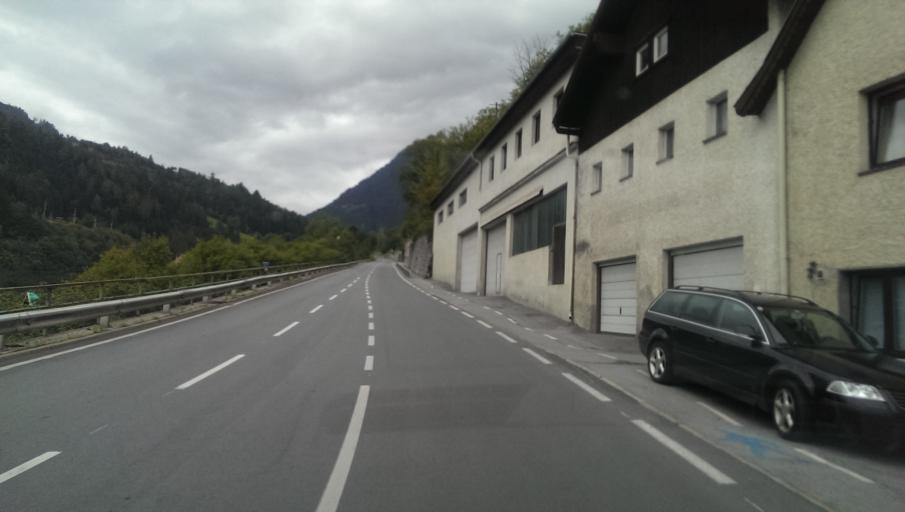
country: AT
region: Tyrol
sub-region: Politischer Bezirk Landeck
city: Pians
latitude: 47.1348
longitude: 10.5109
